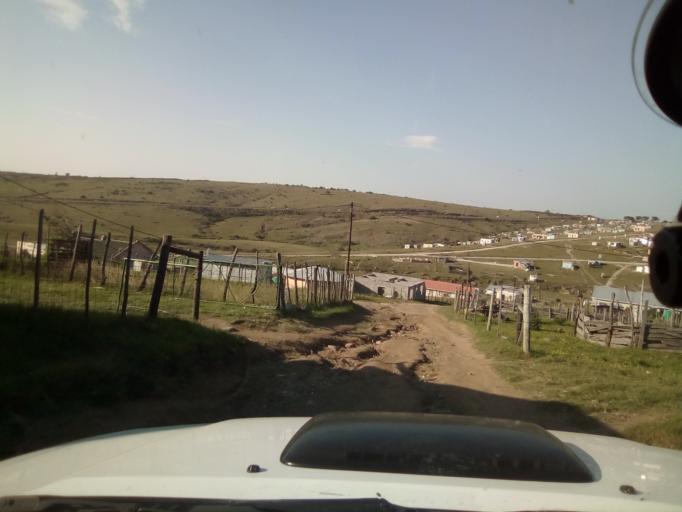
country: ZA
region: Eastern Cape
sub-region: Buffalo City Metropolitan Municipality
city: East London
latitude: -32.8474
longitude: 27.9888
